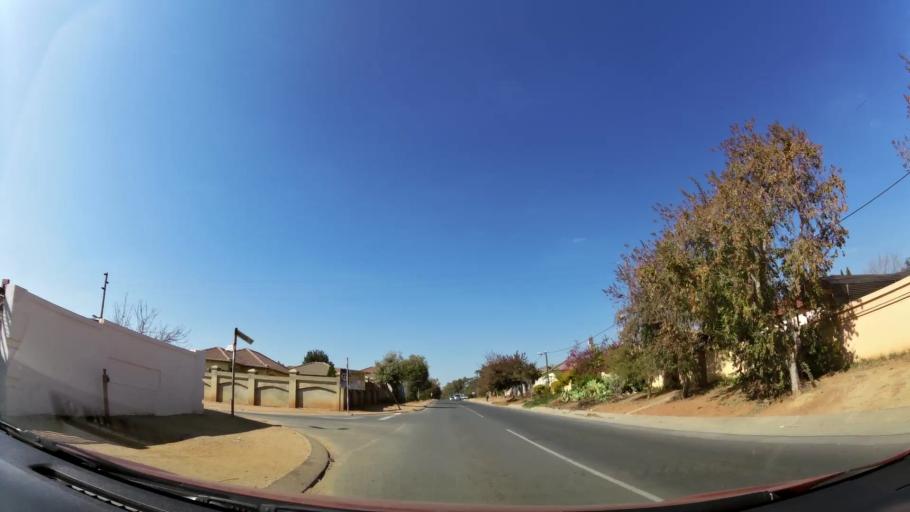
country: ZA
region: Gauteng
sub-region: West Rand District Municipality
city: Muldersdriseloop
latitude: -26.0225
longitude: 27.9377
